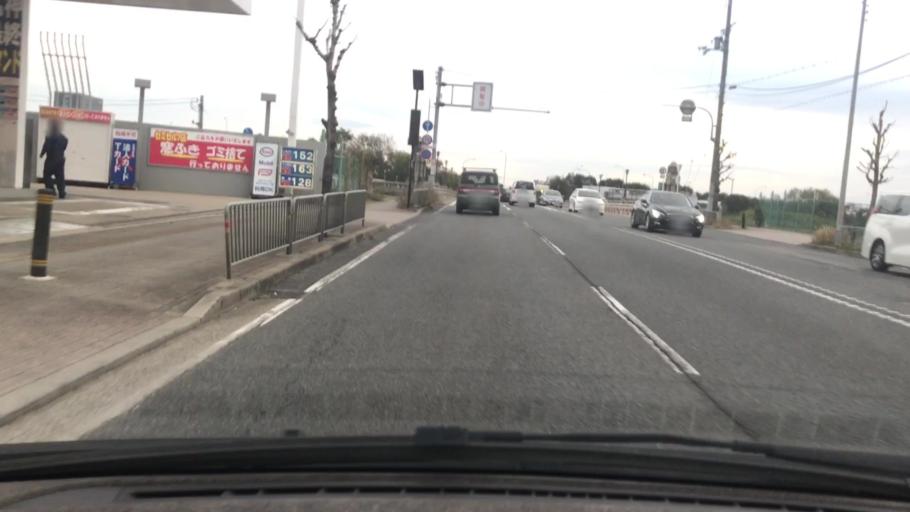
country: JP
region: Kyoto
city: Muko
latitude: 34.9566
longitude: 135.7457
